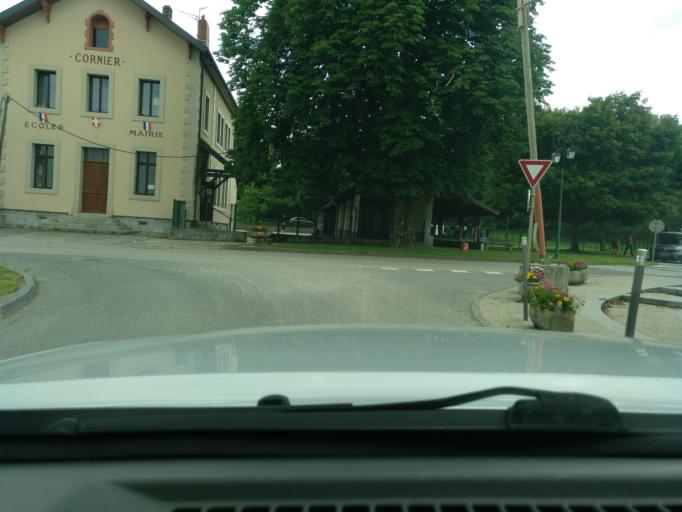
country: FR
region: Rhone-Alpes
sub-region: Departement de la Haute-Savoie
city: Cornier
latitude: 46.0936
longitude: 6.2994
